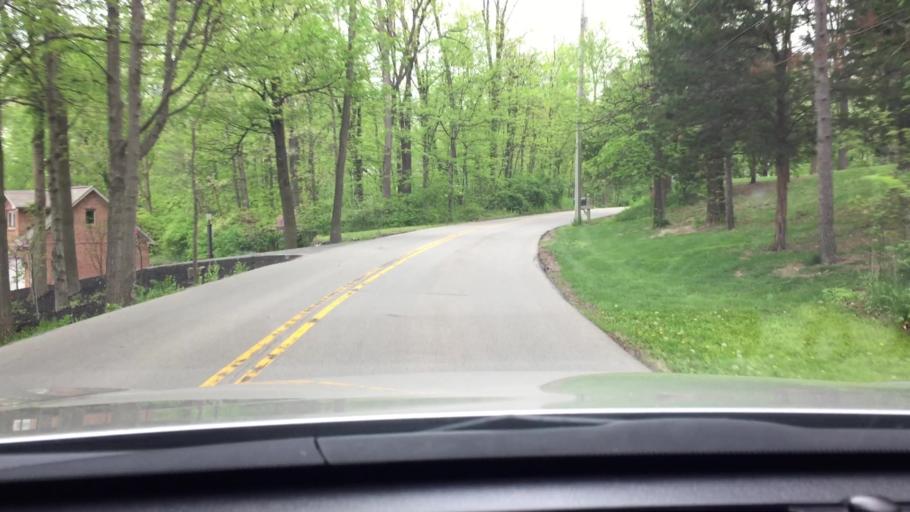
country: US
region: Indiana
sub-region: Hamilton County
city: Carmel
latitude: 39.9968
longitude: -86.0611
